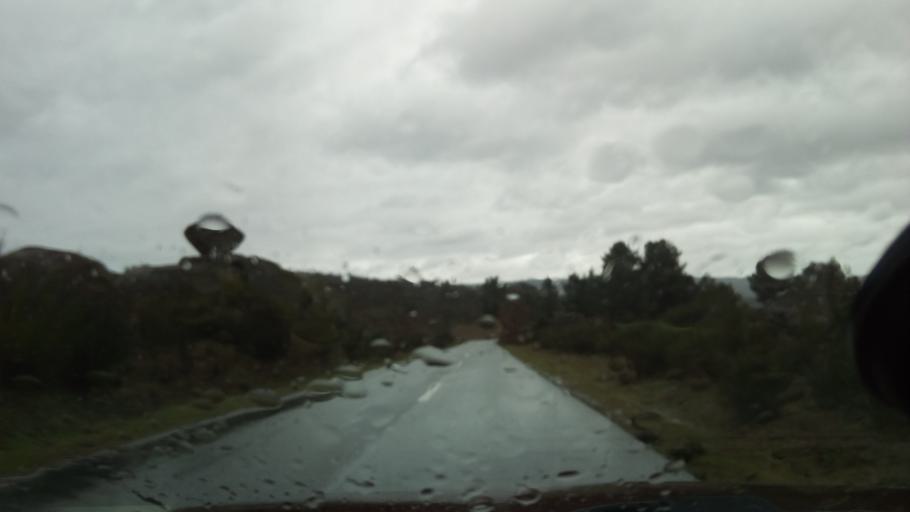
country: PT
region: Guarda
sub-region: Fornos de Algodres
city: Fornos de Algodres
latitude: 40.5774
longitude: -7.5106
